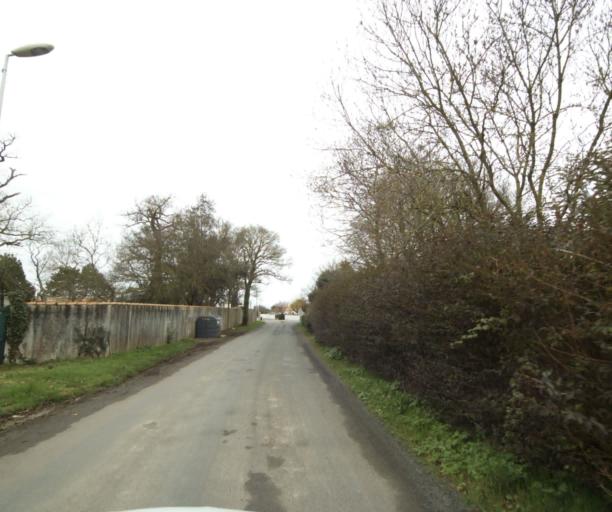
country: FR
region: Poitou-Charentes
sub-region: Departement de la Charente-Maritime
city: Nieul-sur-Mer
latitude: 46.1934
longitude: -1.1711
